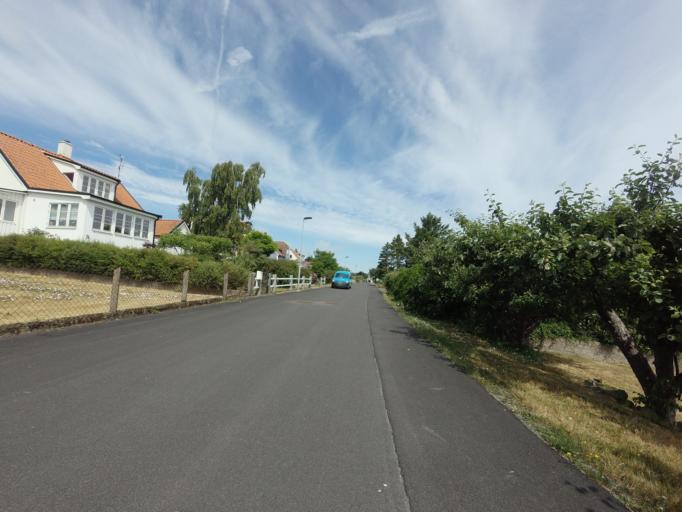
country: SE
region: Skane
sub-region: Simrishamns Kommun
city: Simrishamn
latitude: 55.5453
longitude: 14.3568
